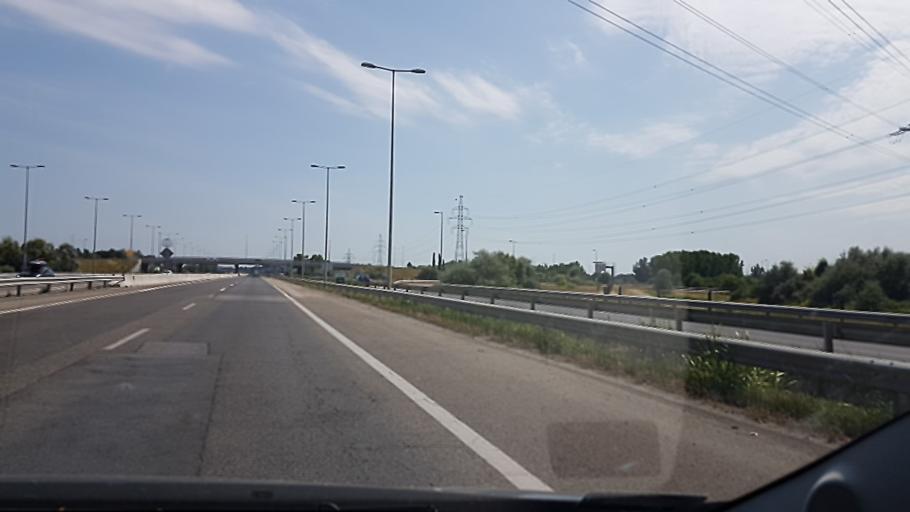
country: HU
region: Budapest
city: Budapest XIX. keruelet
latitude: 47.4278
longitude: 19.1506
